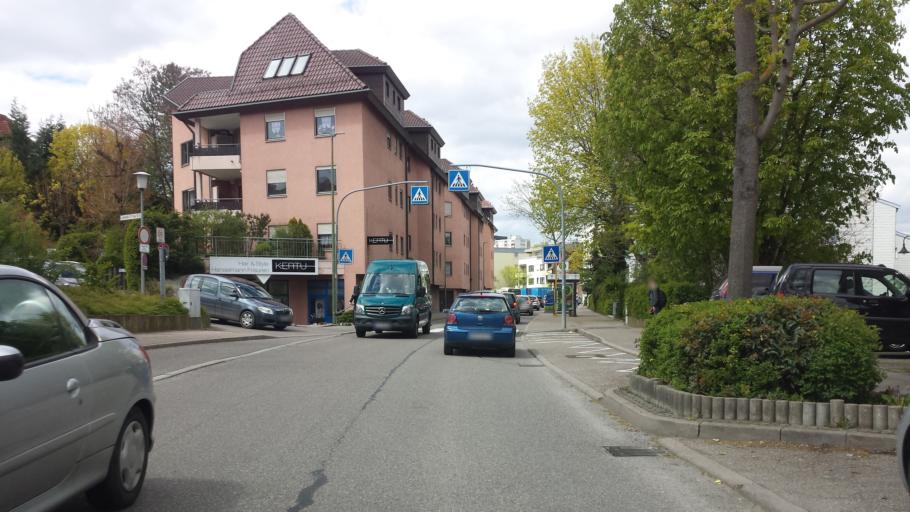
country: DE
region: Baden-Wuerttemberg
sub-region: Regierungsbezirk Stuttgart
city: Leonberg
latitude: 48.8003
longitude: 9.0117
